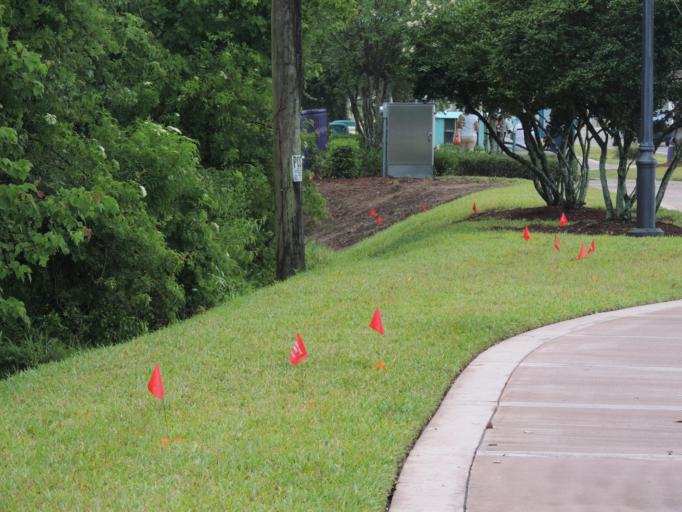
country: US
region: Florida
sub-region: Osceola County
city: Kissimmee
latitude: 28.3210
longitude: -81.4707
